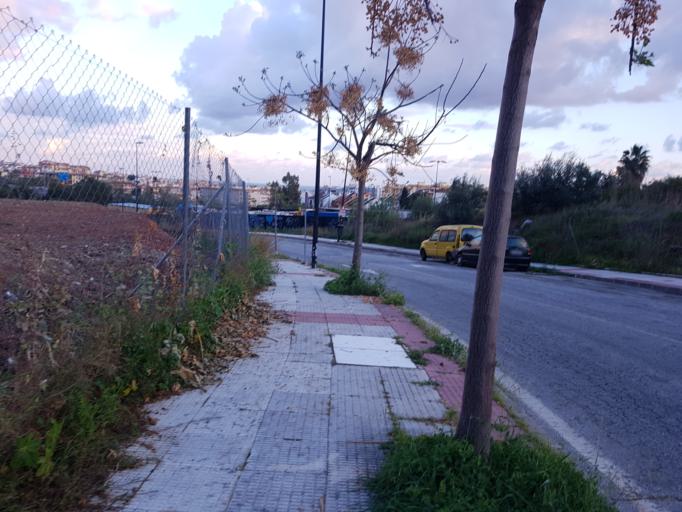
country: ES
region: Andalusia
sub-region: Provincia de Malaga
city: Marbella
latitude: 36.5202
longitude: -4.8910
